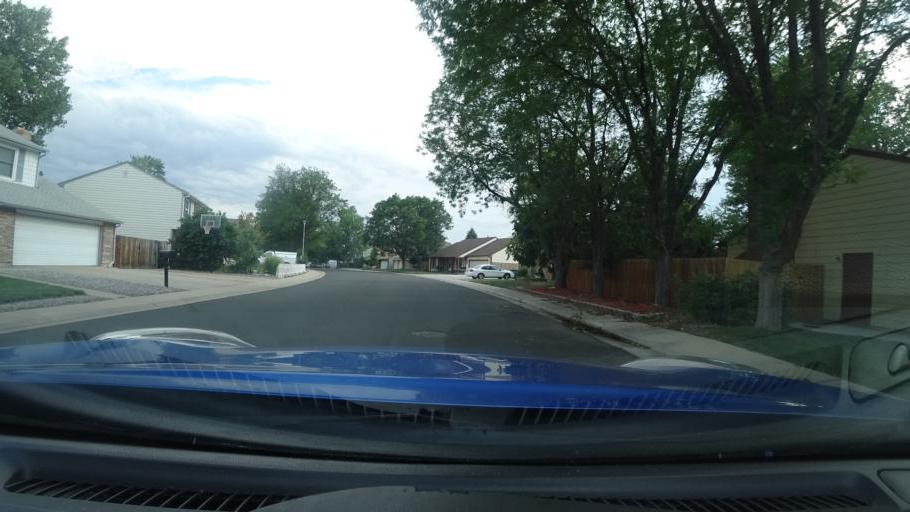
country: US
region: Colorado
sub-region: Adams County
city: Aurora
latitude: 39.6908
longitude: -104.8025
